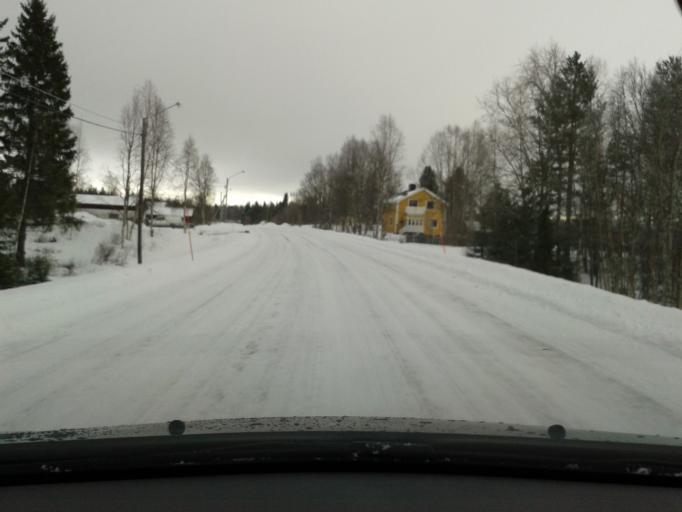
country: SE
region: Vaesterbotten
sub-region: Vilhelmina Kommun
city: Sjoberg
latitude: 64.8358
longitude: 15.9261
